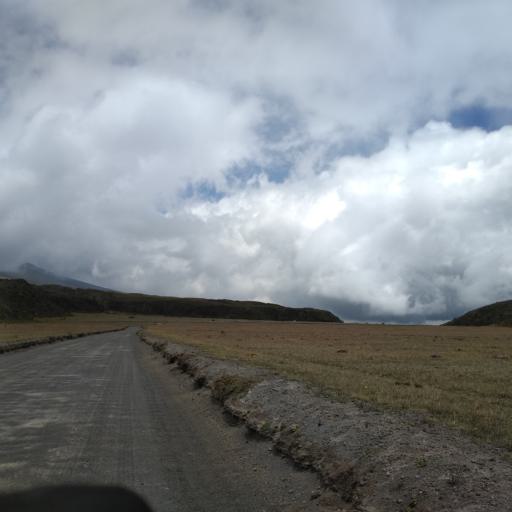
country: EC
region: Pichincha
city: Machachi
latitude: -0.6222
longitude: -78.4745
